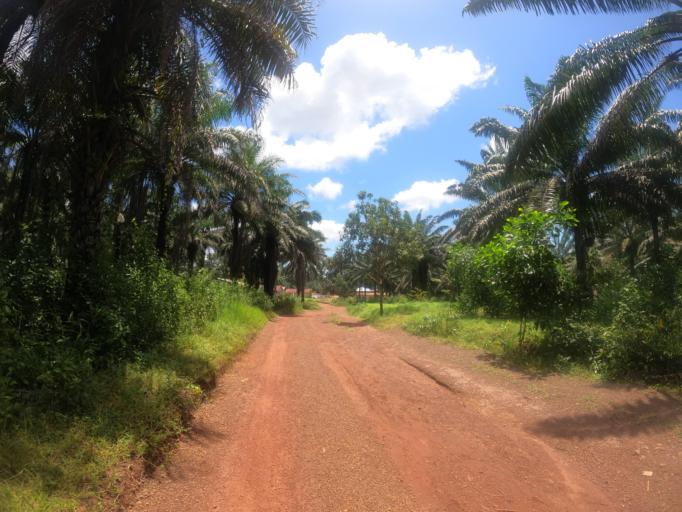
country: SL
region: Northern Province
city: Makeni
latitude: 8.8637
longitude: -12.1071
